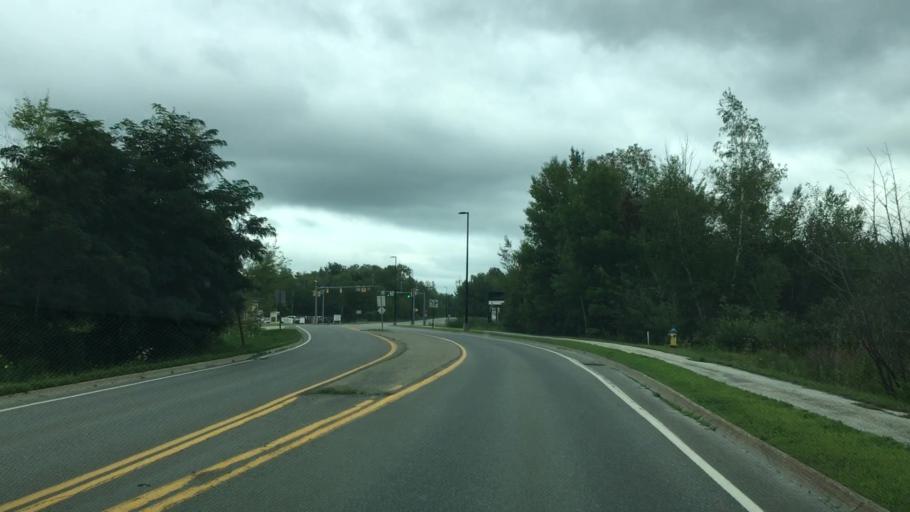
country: US
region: Maine
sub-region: Penobscot County
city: Brewer
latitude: 44.7759
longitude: -68.7412
